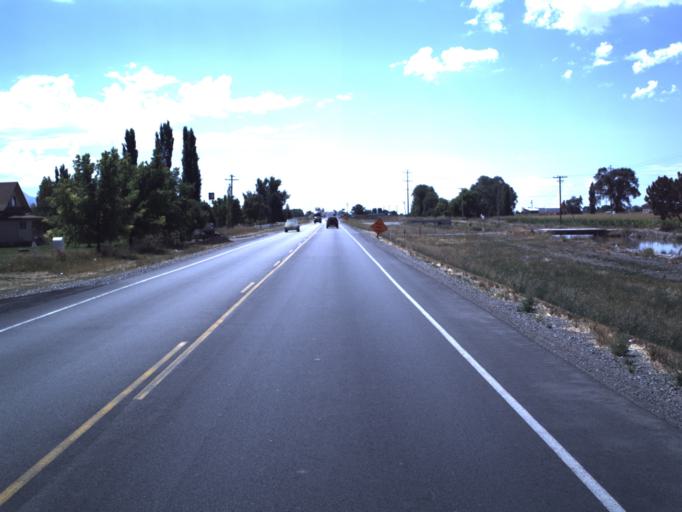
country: US
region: Utah
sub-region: Box Elder County
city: Elwood
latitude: 41.6879
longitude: -112.1415
